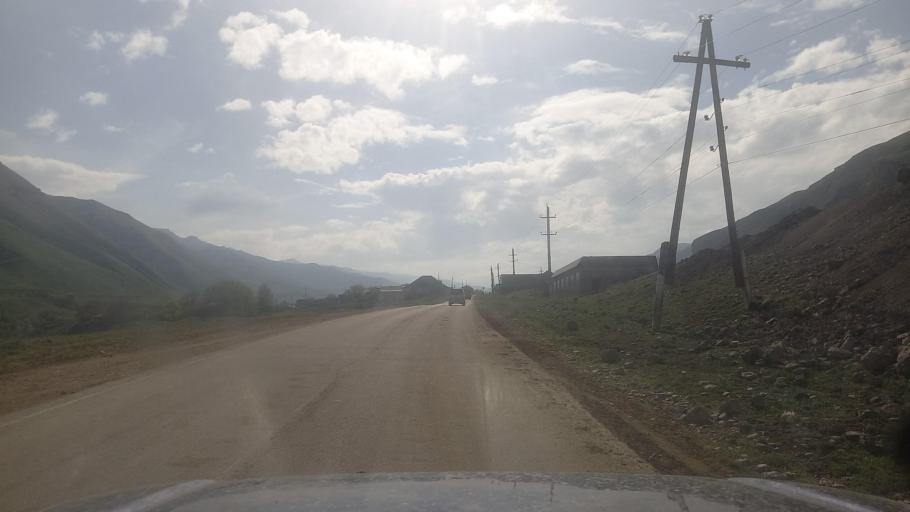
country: RU
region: Kabardino-Balkariya
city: Kamennomostskoye
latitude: 43.7329
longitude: 42.9619
